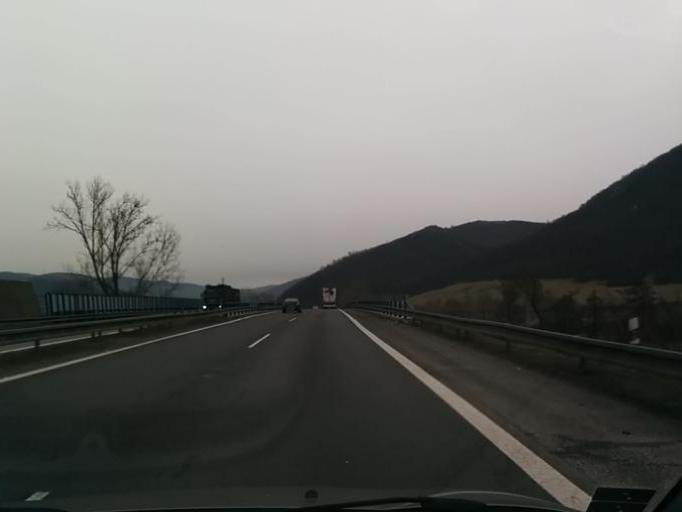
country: SK
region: Banskobystricky
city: Ziar nad Hronom
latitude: 48.5880
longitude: 18.9048
